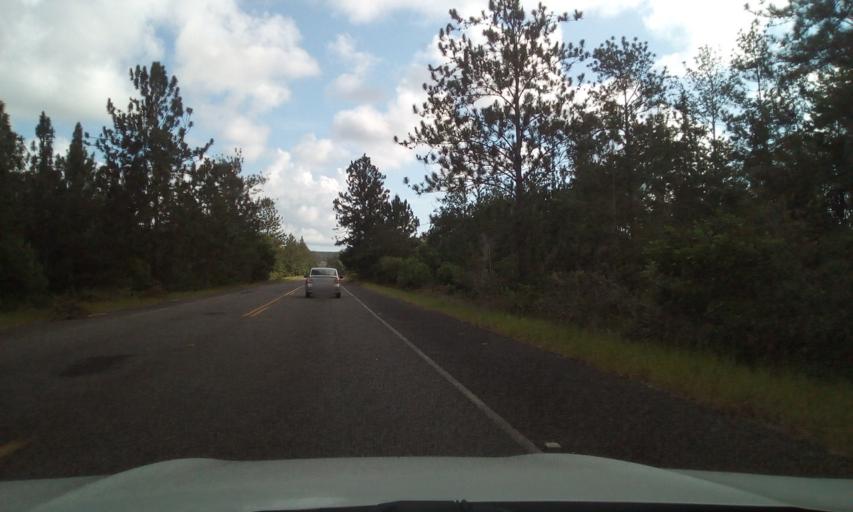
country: BR
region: Bahia
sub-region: Entre Rios
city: Entre Rios
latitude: -12.1513
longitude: -37.8003
